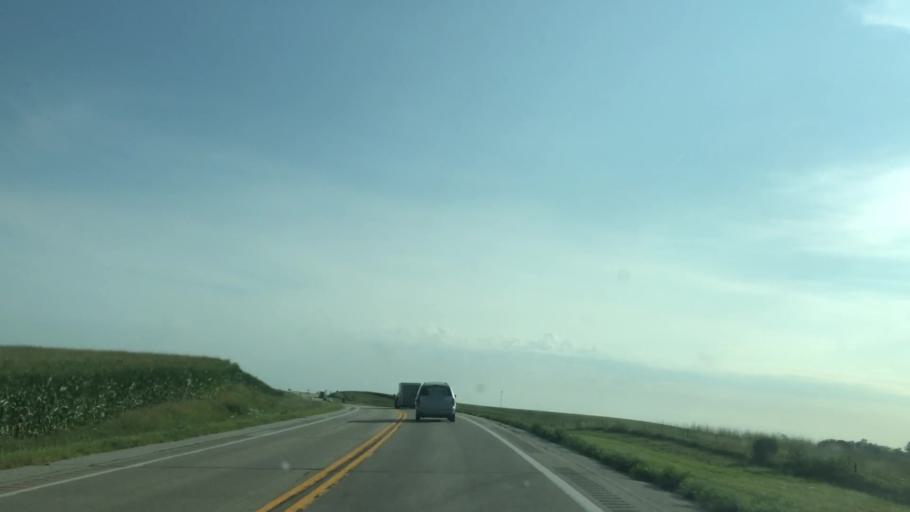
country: US
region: Iowa
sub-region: Marshall County
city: Marshalltown
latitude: 42.0212
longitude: -93.0101
